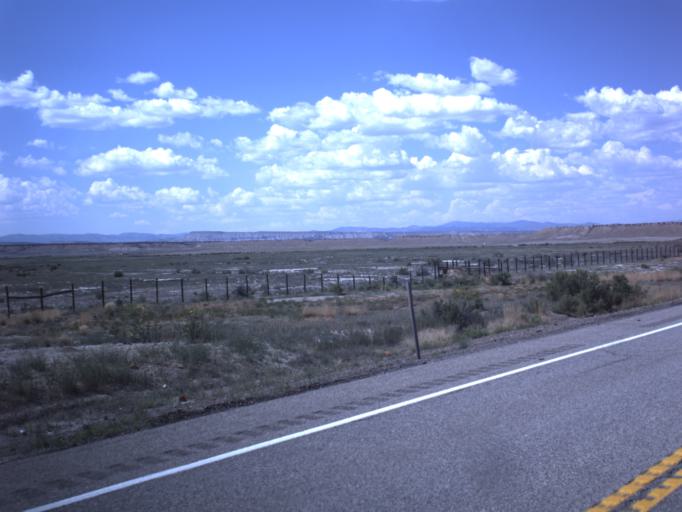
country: US
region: Utah
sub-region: Emery County
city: Huntington
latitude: 39.4461
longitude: -110.8639
